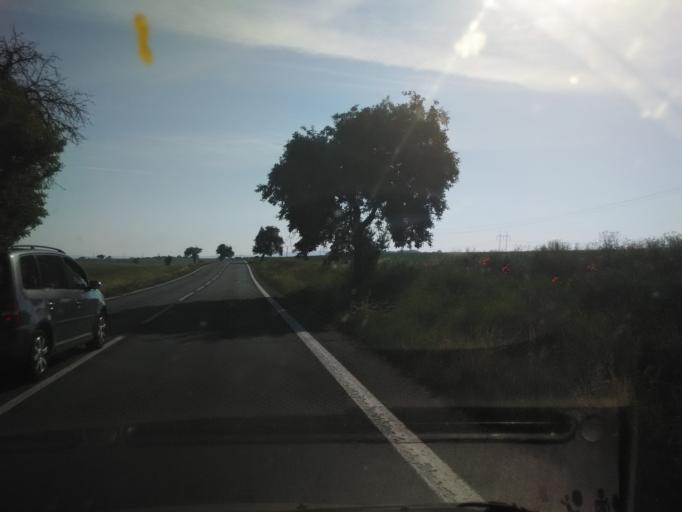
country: SK
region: Nitriansky
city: Levice
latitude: 48.2400
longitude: 18.6729
